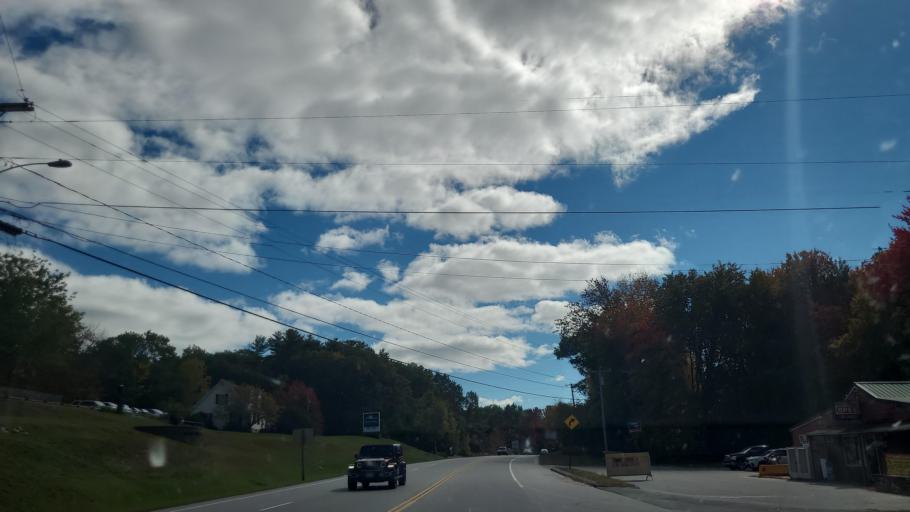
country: US
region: Maine
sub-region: Cumberland County
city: Raymond
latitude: 43.9422
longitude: -70.5465
